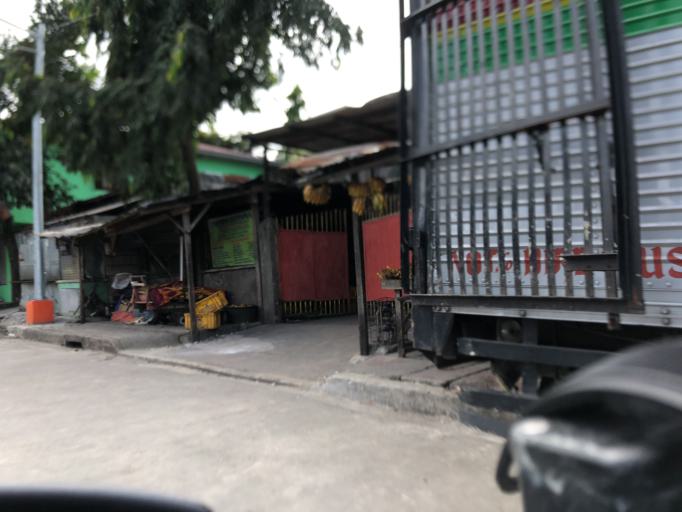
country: PH
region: Central Luzon
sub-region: Province of Bulacan
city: San Jose del Monte
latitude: 14.7519
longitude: 121.0572
